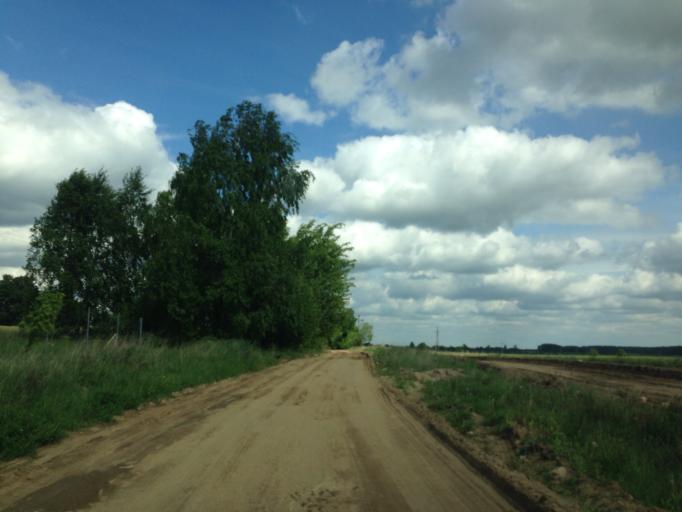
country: PL
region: Warmian-Masurian Voivodeship
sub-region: Powiat nidzicki
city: Kozlowo
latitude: 53.4396
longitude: 20.3115
